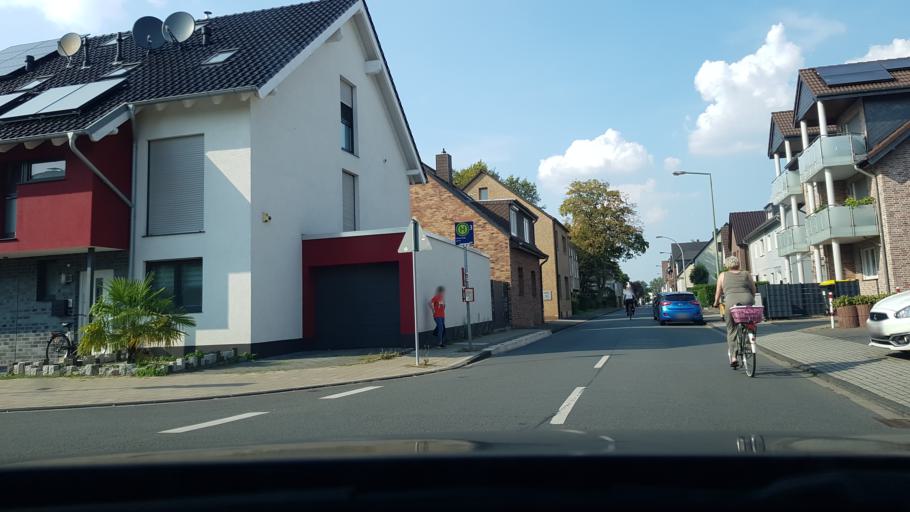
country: DE
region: North Rhine-Westphalia
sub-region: Regierungsbezirk Dusseldorf
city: Hochfeld
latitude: 51.3792
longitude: 6.7655
